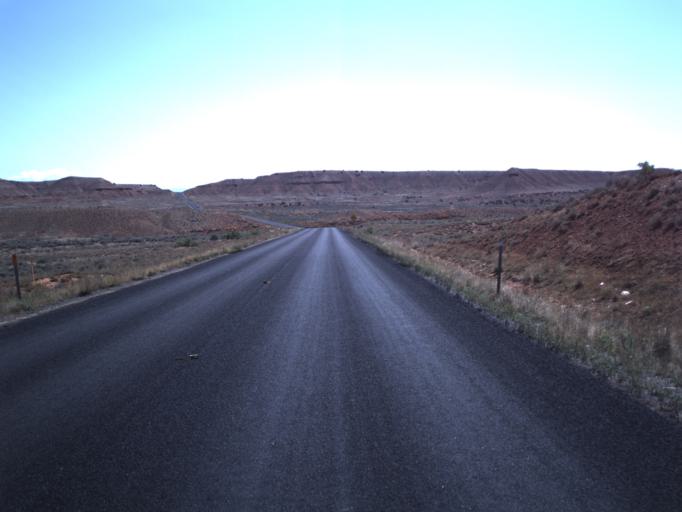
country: US
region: Utah
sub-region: Uintah County
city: Maeser
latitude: 40.4129
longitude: -109.7380
